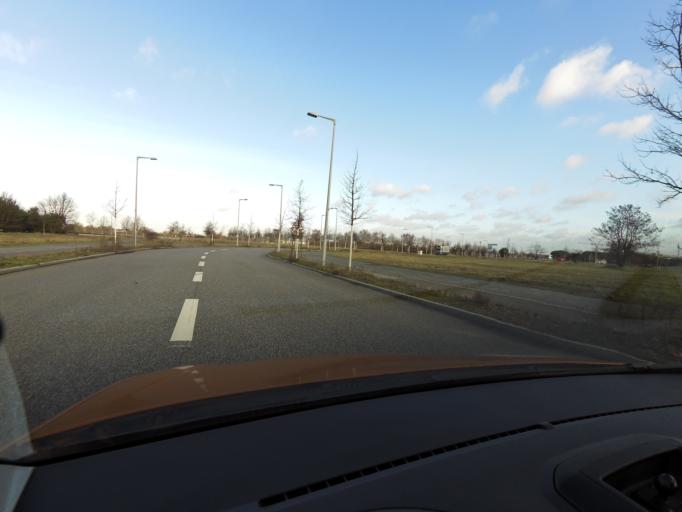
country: DE
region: Berlin
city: Johannisthal
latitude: 52.4322
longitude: 13.5183
